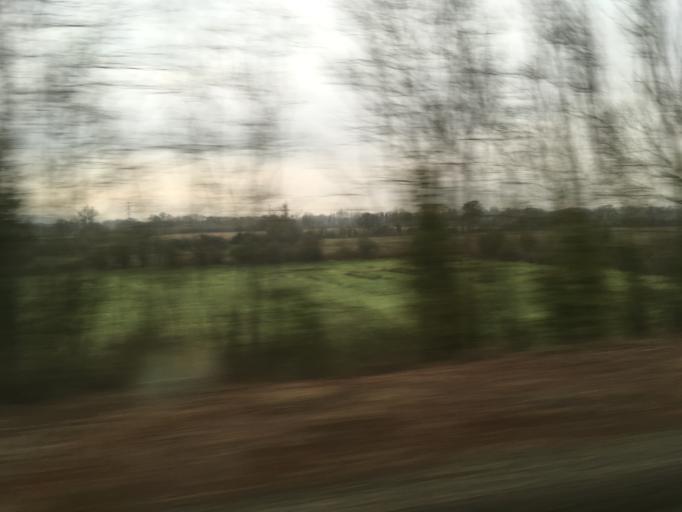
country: GB
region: England
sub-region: Wiltshire
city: Charlton
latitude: 51.5563
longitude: -2.0454
